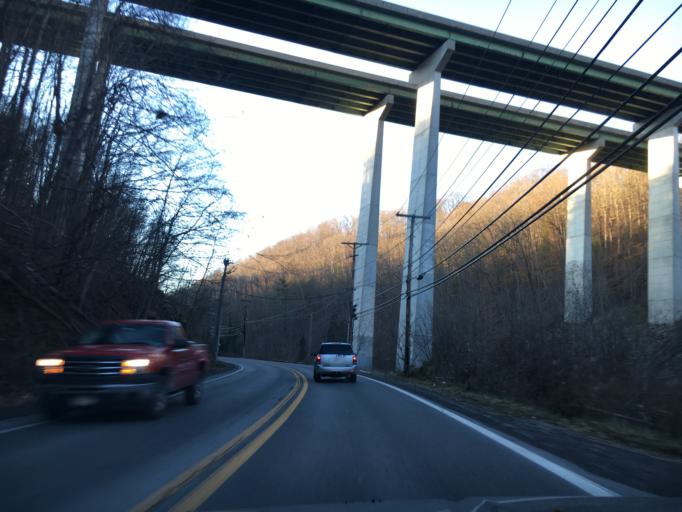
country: US
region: West Virginia
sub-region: Raleigh County
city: Beaver
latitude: 37.7550
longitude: -81.1500
